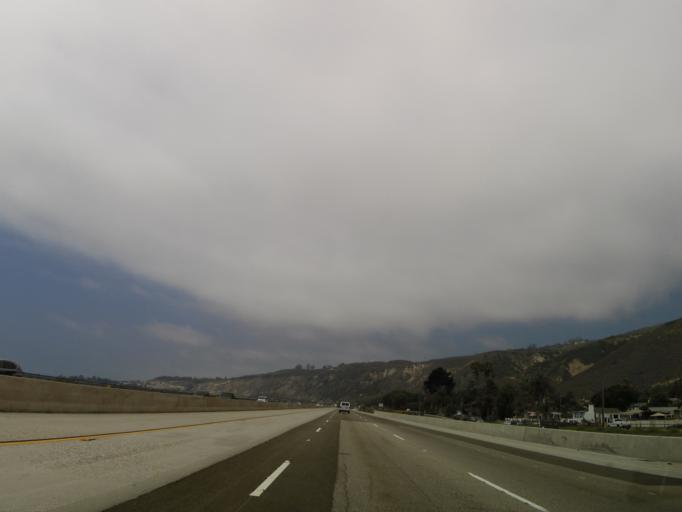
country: US
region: California
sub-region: Santa Barbara County
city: Carpinteria
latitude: 34.3622
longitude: -119.4475
